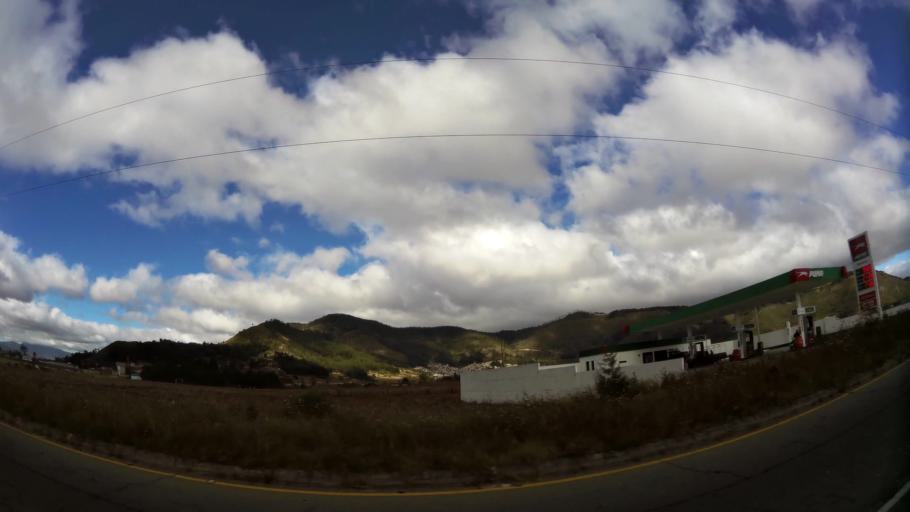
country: GT
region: Quetzaltenango
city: Salcaja
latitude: 14.8885
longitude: -91.4673
